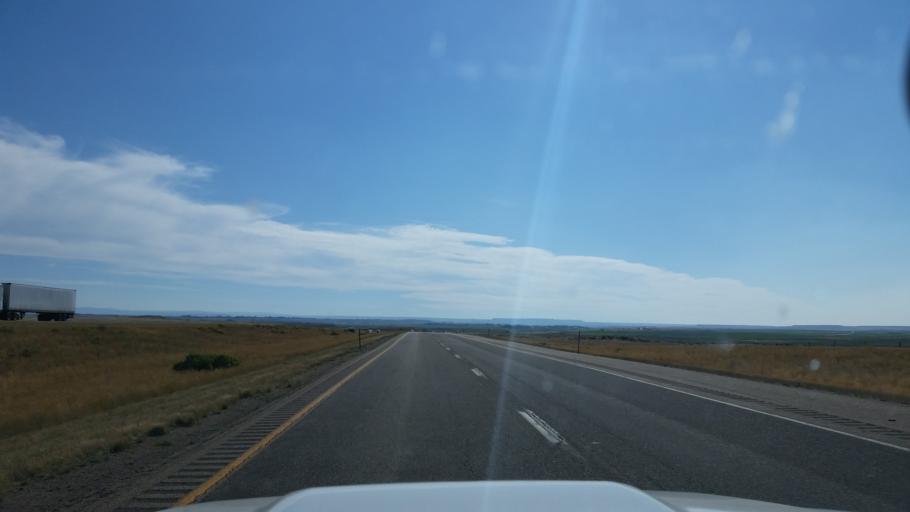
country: US
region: Wyoming
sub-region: Uinta County
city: Lyman
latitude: 41.3819
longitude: -110.2283
